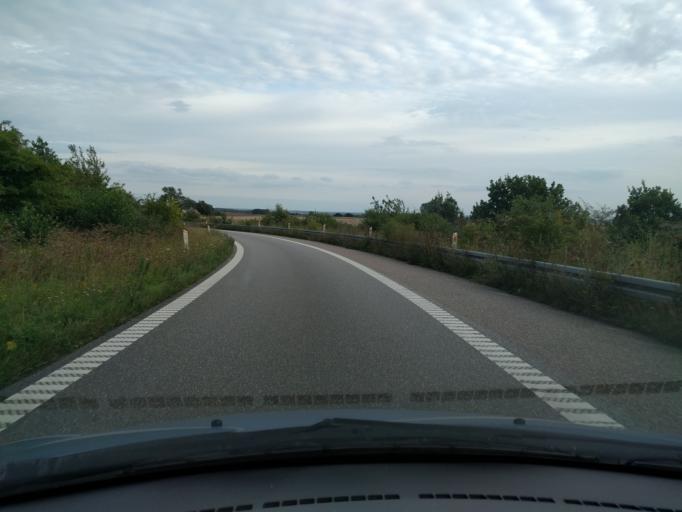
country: DK
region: Zealand
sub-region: Vordingborg Kommune
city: Nyrad
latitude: 54.9996
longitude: 11.9913
